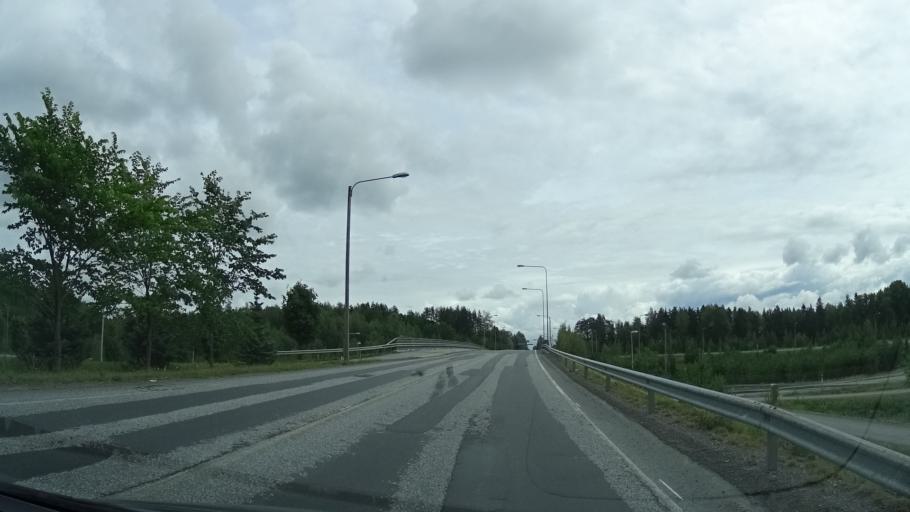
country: FI
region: Pirkanmaa
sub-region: Etelae-Pirkanmaa
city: Urjala
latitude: 61.0819
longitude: 23.5338
